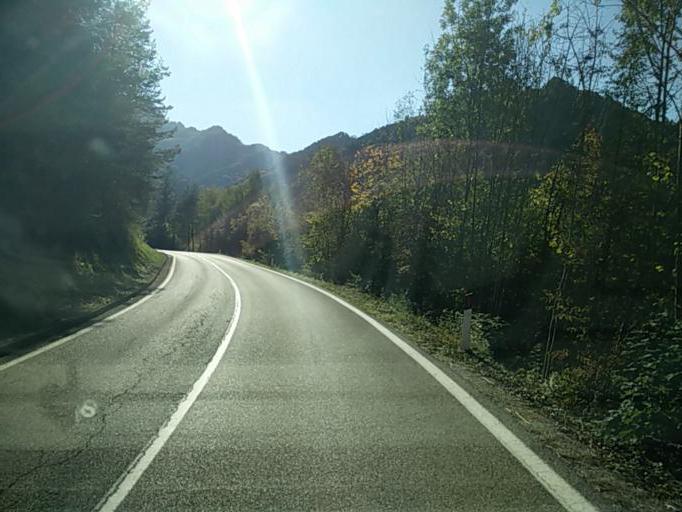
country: IT
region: Lombardy
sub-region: Provincia di Brescia
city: Anfo
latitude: 45.7480
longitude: 10.5031
